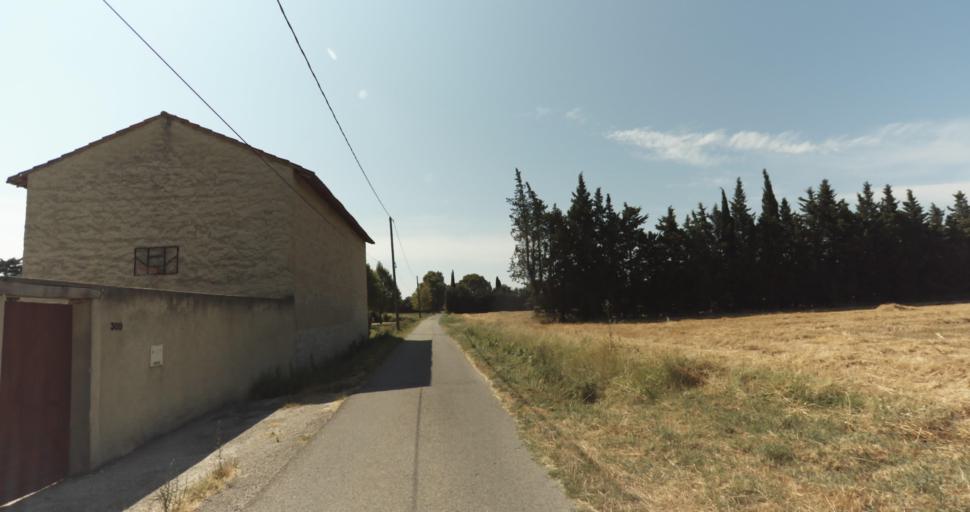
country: FR
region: Provence-Alpes-Cote d'Azur
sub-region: Departement du Vaucluse
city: Monteux
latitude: 44.0178
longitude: 4.9995
